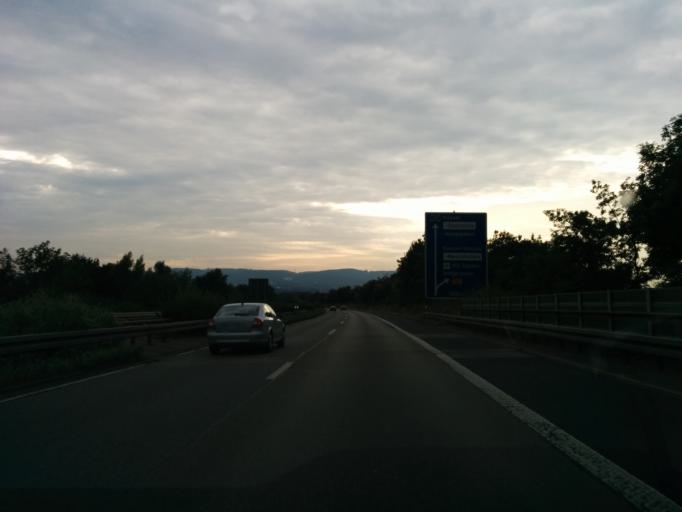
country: DE
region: Hesse
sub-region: Regierungsbezirk Kassel
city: Lohfelden
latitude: 51.2861
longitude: 9.5138
